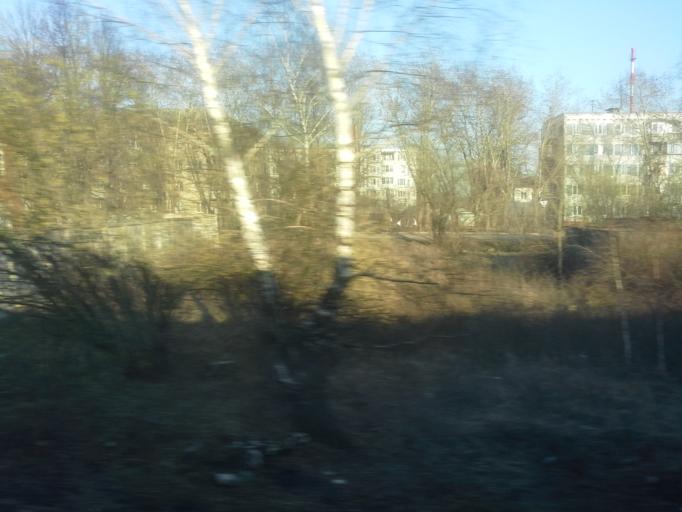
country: RU
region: Moskovskaya
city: Nekrasovskiy
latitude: 56.0873
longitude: 37.5025
